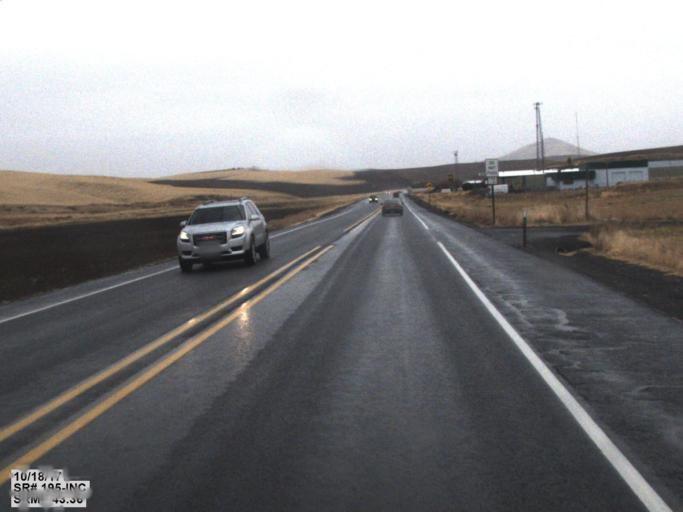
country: US
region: Washington
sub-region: Whitman County
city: Colfax
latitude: 46.9507
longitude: -117.3341
